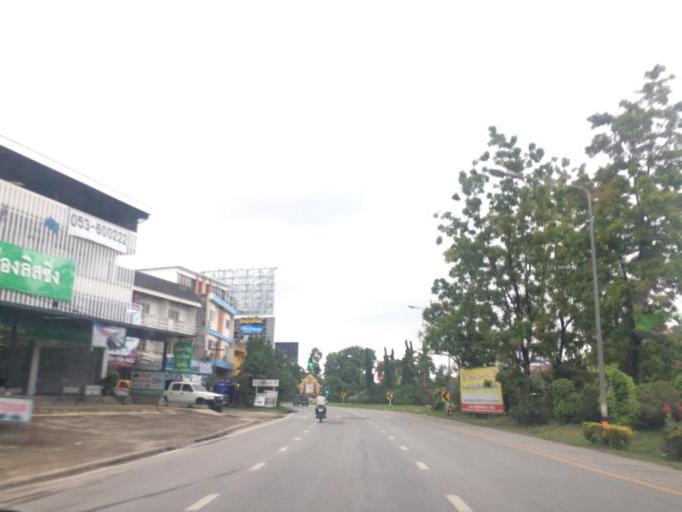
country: TH
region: Chiang Rai
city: Chiang Rai
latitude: 19.9070
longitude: 99.8408
